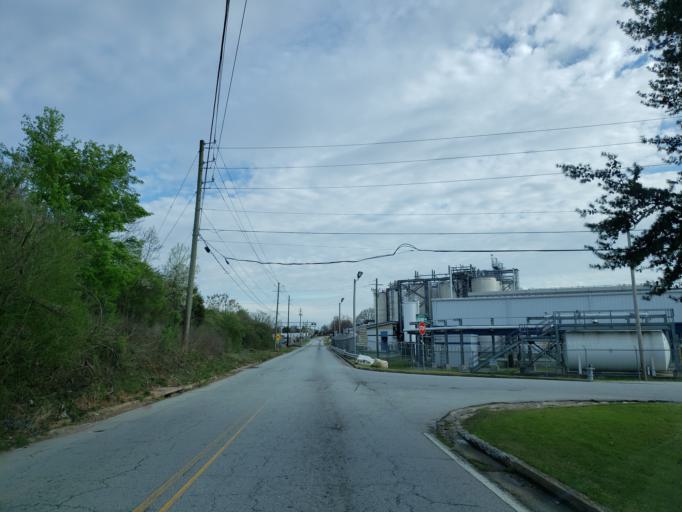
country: US
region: Georgia
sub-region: Clayton County
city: Forest Park
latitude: 33.6302
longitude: -84.3876
